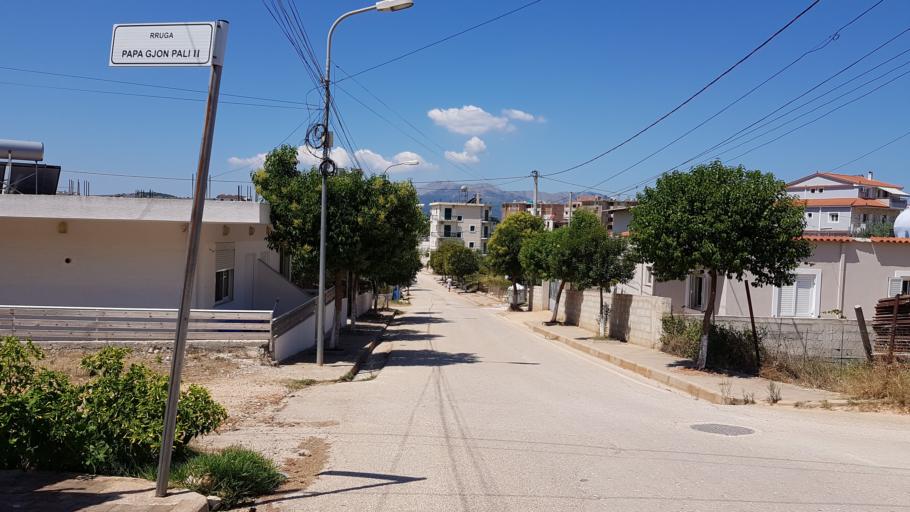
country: AL
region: Vlore
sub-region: Rrethi i Sarandes
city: Xarre
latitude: 39.7728
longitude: 20.0082
